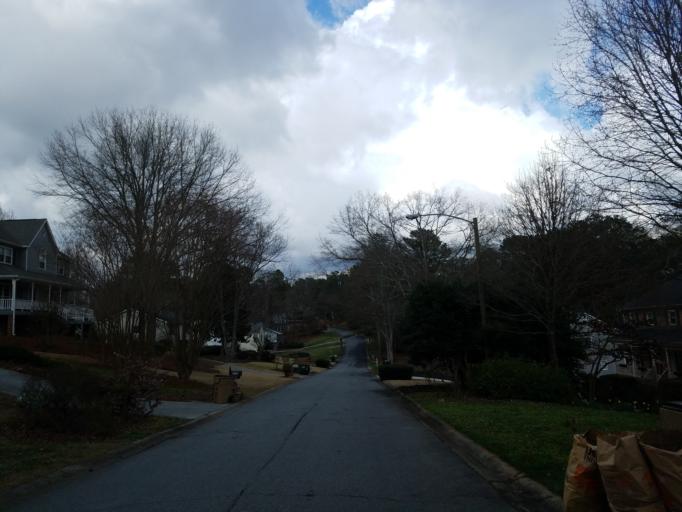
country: US
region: Georgia
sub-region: Cherokee County
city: Woodstock
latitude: 34.0400
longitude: -84.4890
